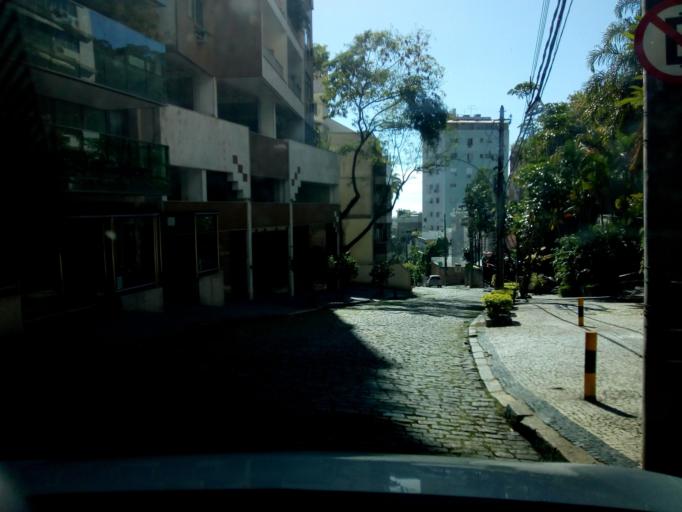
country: BR
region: Rio de Janeiro
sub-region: Rio De Janeiro
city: Rio de Janeiro
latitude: -22.9862
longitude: -43.2339
